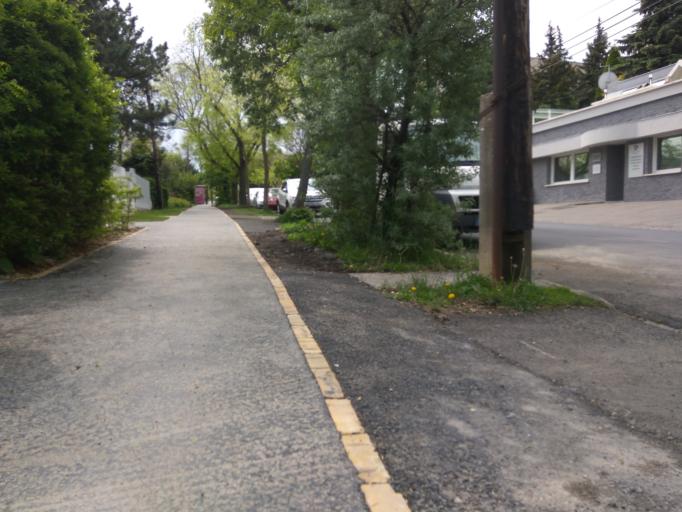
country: HU
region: Budapest
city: Budapest XII. keruelet
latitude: 47.4913
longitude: 19.0023
